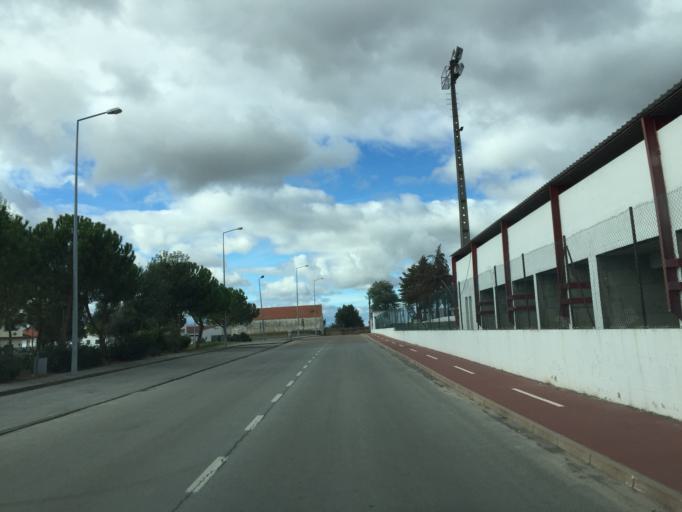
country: PT
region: Portalegre
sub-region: Alter do Chao
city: Alter do Chao
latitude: 39.1979
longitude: -7.6631
